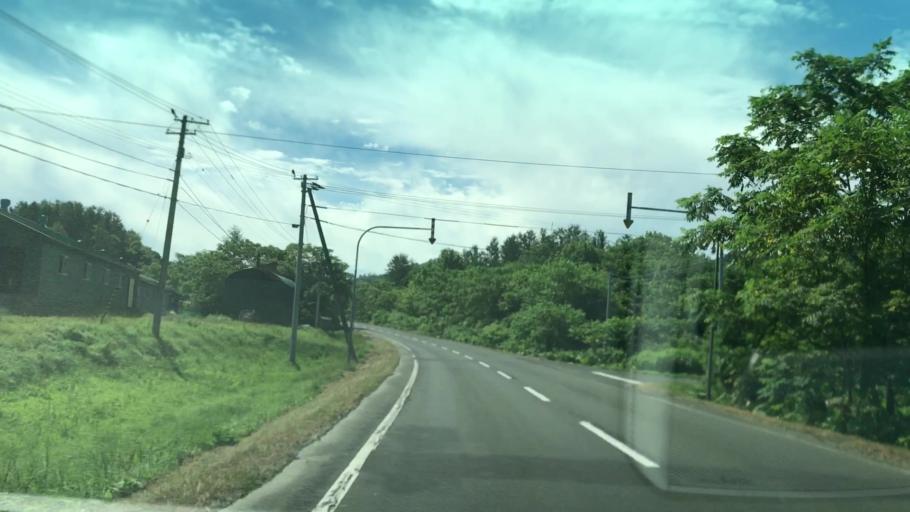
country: JP
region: Hokkaido
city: Shimo-furano
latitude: 42.9594
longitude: 142.4286
